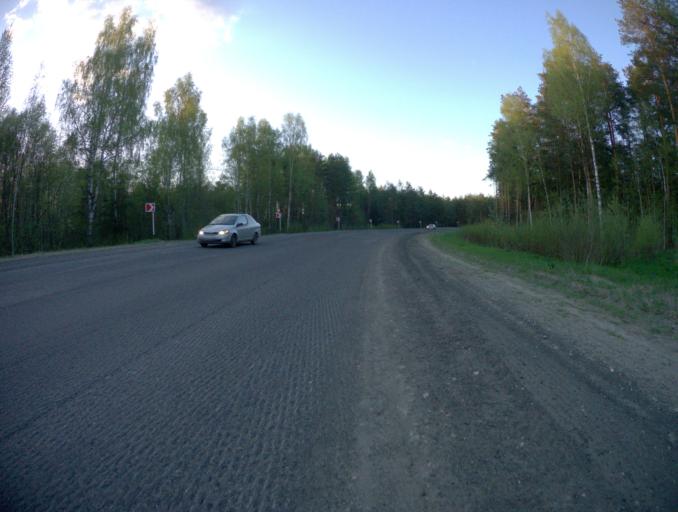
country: RU
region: Vladimir
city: Kommunar
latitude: 56.0930
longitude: 40.4374
